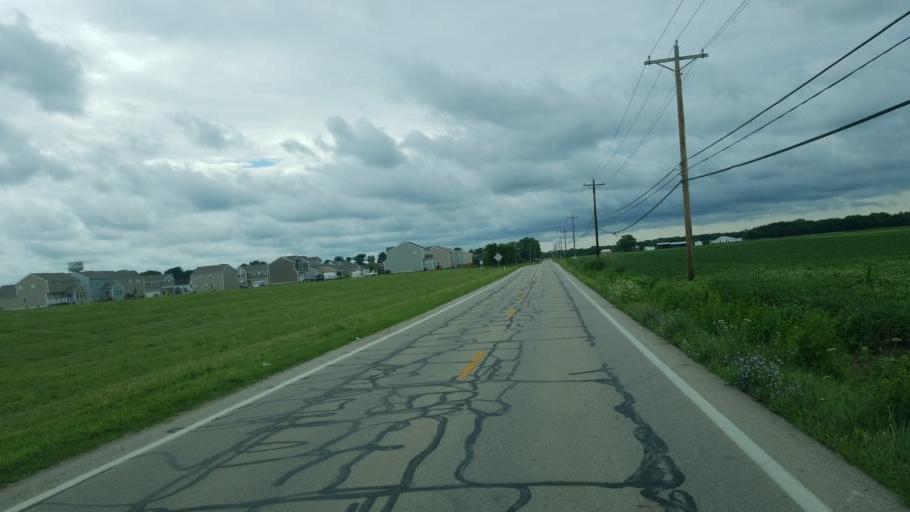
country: US
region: Ohio
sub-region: Pickaway County
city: South Bloomfield
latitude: 39.7190
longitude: -82.9951
